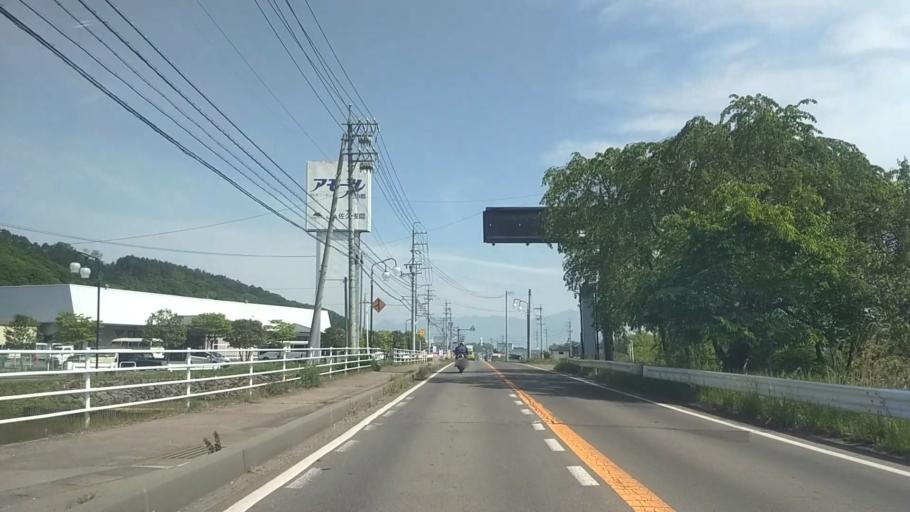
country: JP
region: Nagano
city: Saku
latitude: 36.1700
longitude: 138.4859
